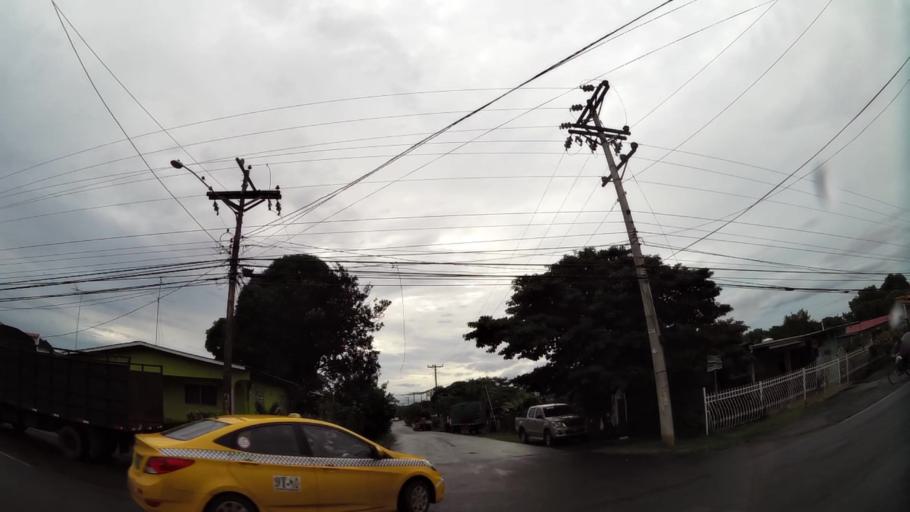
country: PA
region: Veraguas
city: Santiago de Veraguas
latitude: 8.1077
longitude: -80.9774
